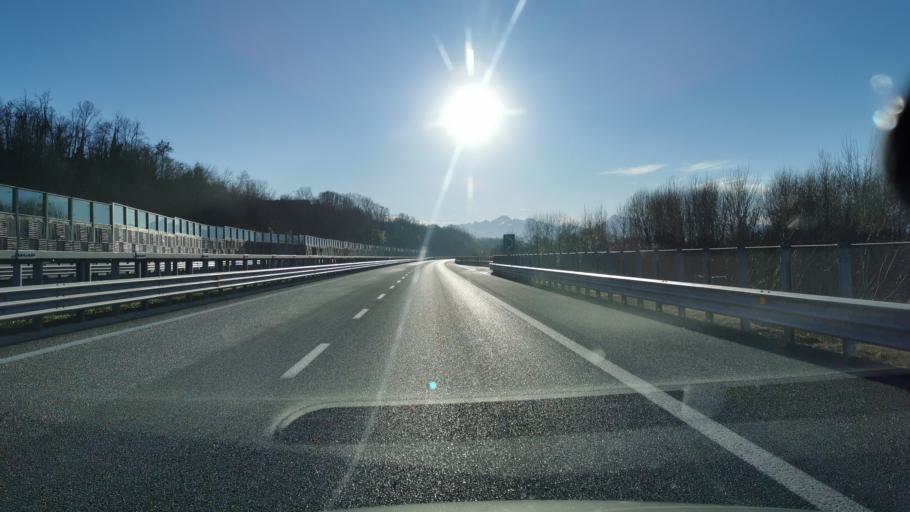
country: IT
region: Piedmont
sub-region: Provincia di Cuneo
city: Montanera
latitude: 44.4638
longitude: 7.6633
